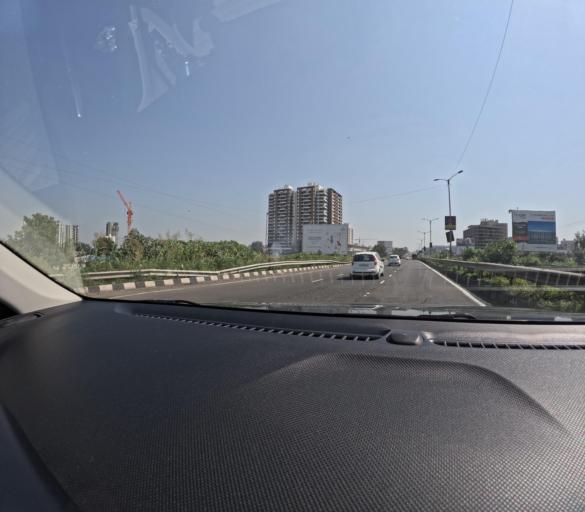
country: IN
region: Maharashtra
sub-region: Pune Division
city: Pimpri
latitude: 18.6323
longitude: 73.7408
